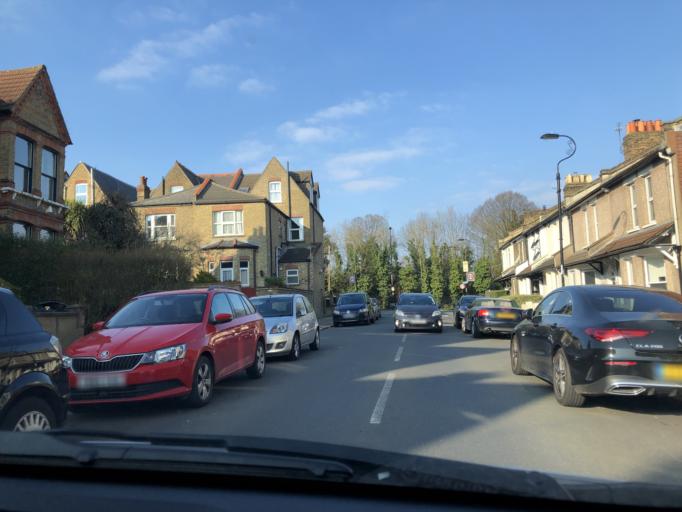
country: GB
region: England
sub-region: Greater London
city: Catford
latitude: 51.4493
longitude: -0.0471
